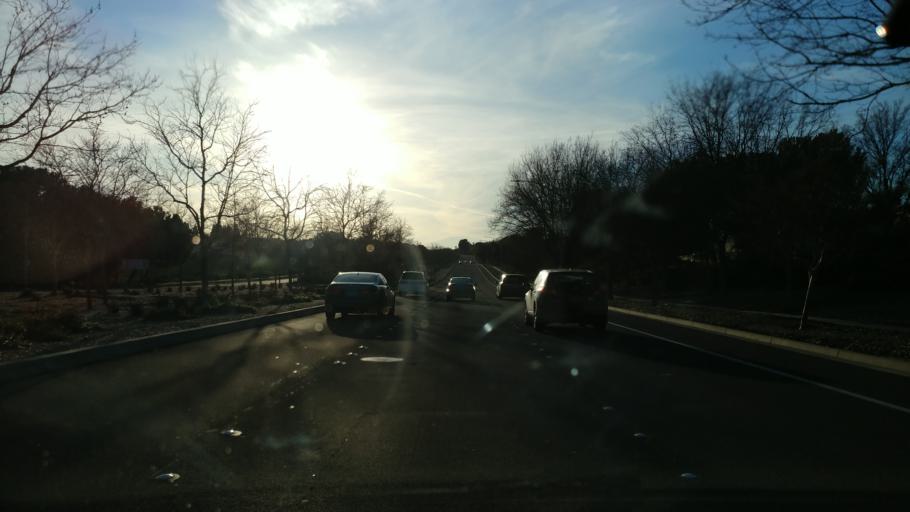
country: US
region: California
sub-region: Contra Costa County
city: San Ramon
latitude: 37.7723
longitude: -121.9331
